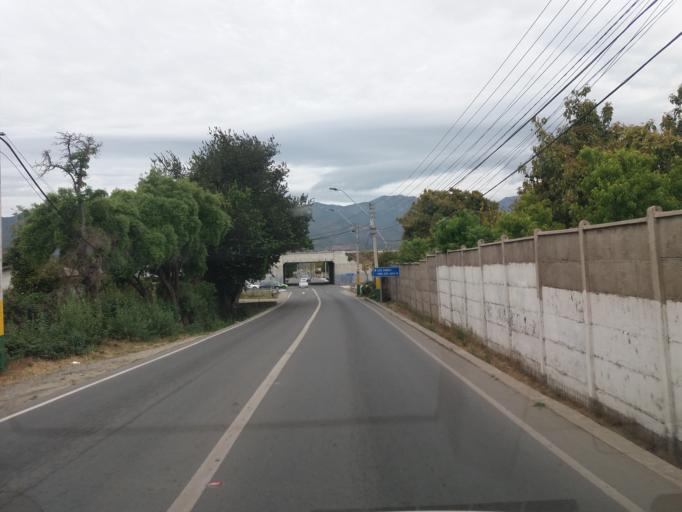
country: CL
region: Valparaiso
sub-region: Provincia de Quillota
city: Quillota
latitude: -32.8428
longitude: -71.2250
